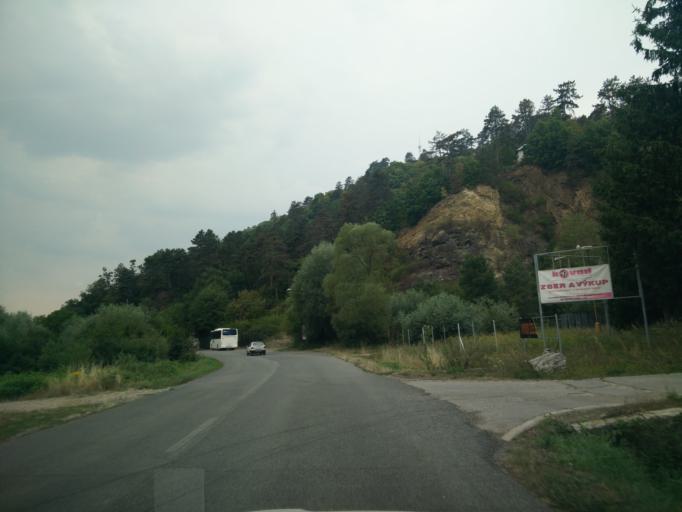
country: SK
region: Banskobystricky
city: Ziar nad Hronom
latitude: 48.5920
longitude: 18.8791
